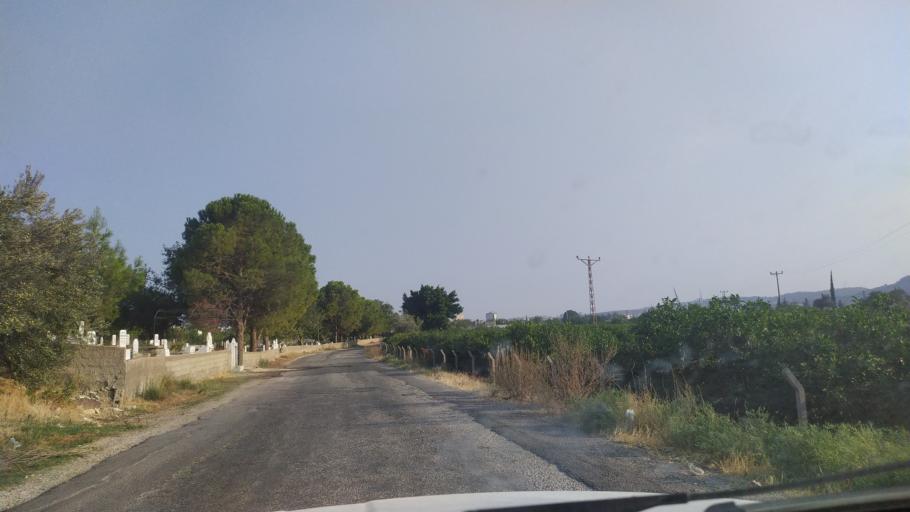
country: TR
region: Mersin
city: Silifke
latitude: 36.4014
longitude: 33.9260
